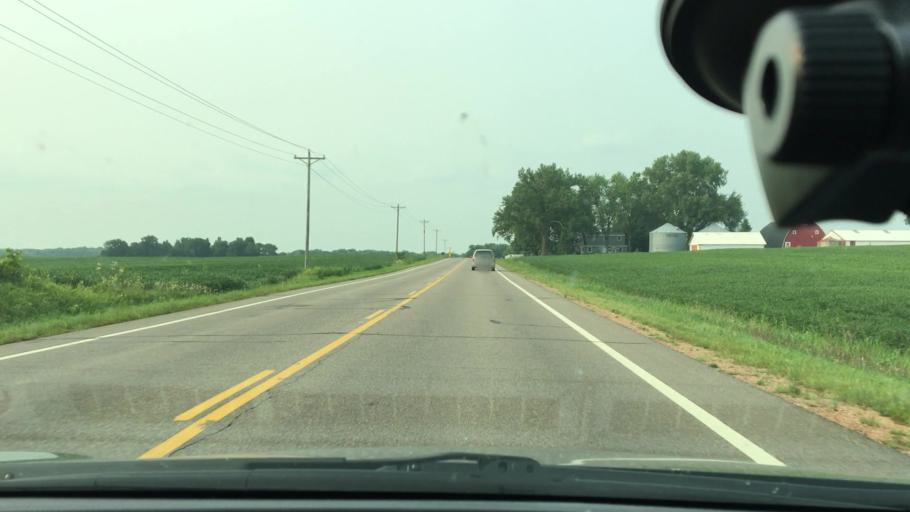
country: US
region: Minnesota
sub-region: Hennepin County
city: Champlin
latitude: 45.1827
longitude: -93.4623
